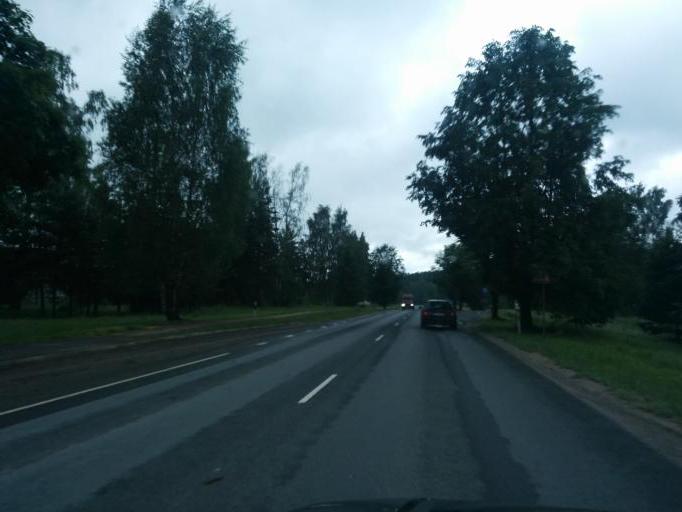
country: LV
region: Smiltene
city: Smiltene
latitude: 57.4135
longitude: 25.9344
